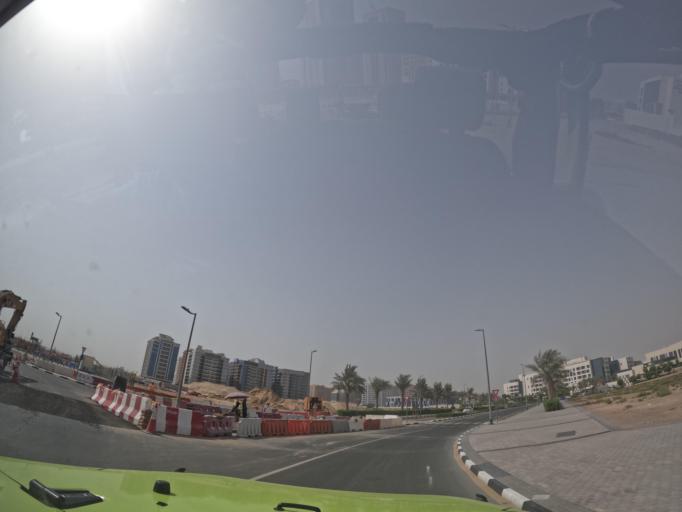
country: AE
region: Dubai
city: Dubai
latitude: 25.1172
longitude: 55.3745
